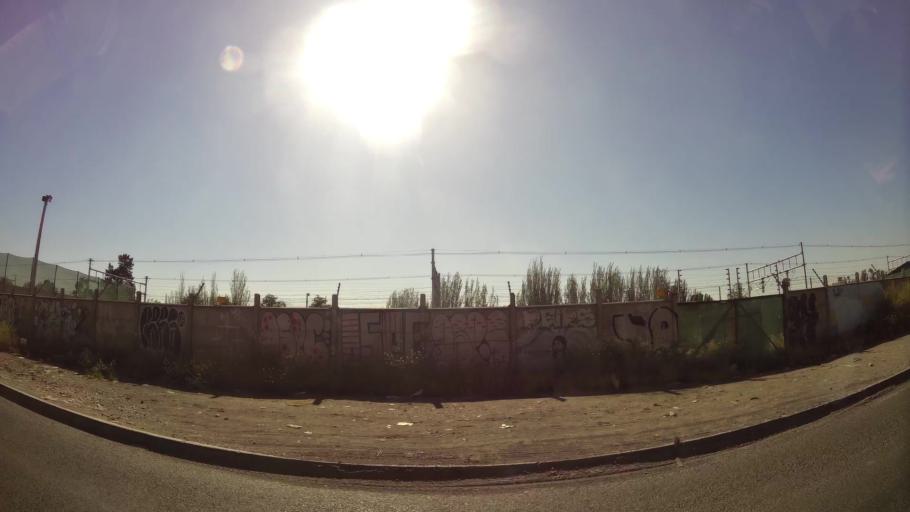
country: CL
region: Santiago Metropolitan
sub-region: Provincia de Maipo
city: San Bernardo
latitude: -33.5611
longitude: -70.6967
